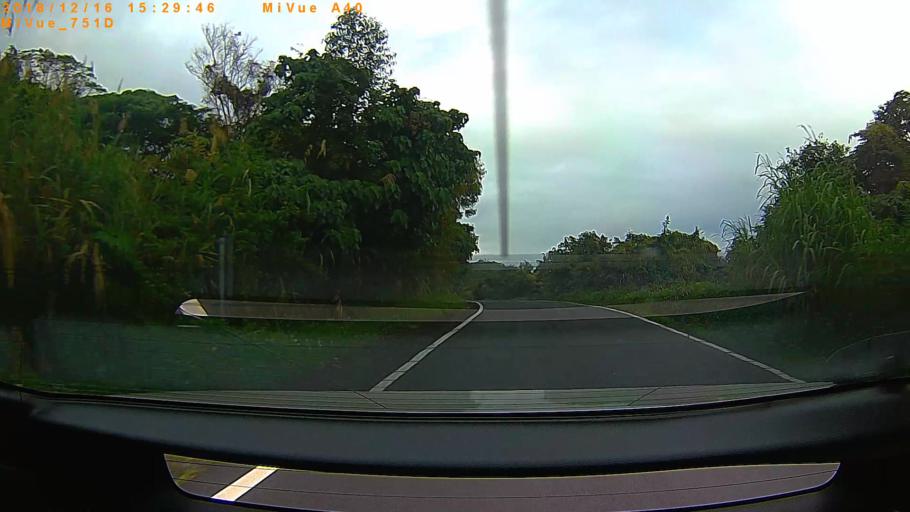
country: TW
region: Taiwan
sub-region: Hualien
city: Hualian
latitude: 23.9133
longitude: 121.5996
